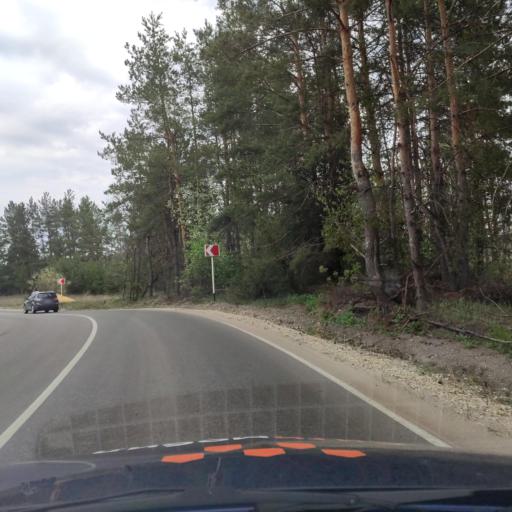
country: RU
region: Voronezj
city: Podgornoye
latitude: 51.8319
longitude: 39.1441
